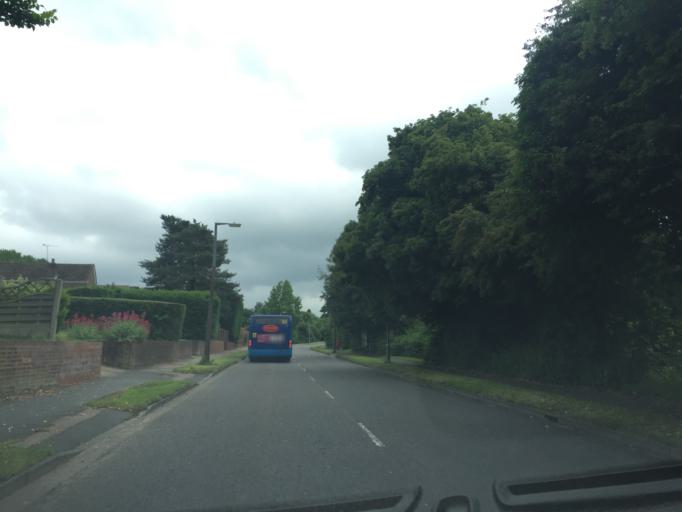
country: GB
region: England
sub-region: Essex
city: Harlow
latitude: 51.7544
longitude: 0.0808
